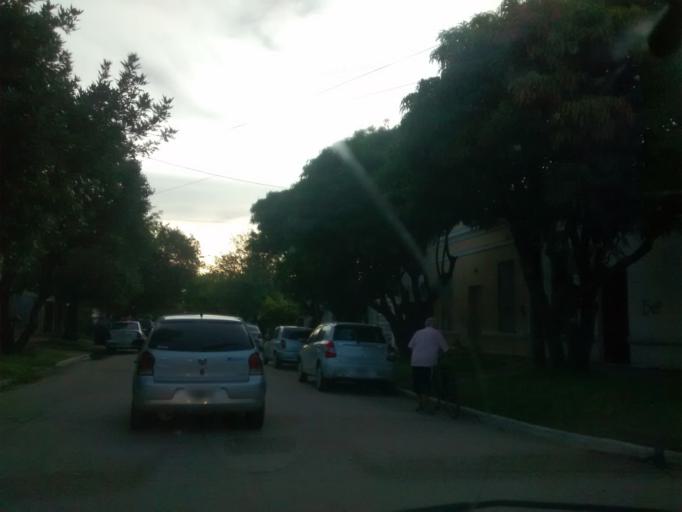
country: AR
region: Chaco
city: Resistencia
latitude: -27.4392
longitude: -58.9964
